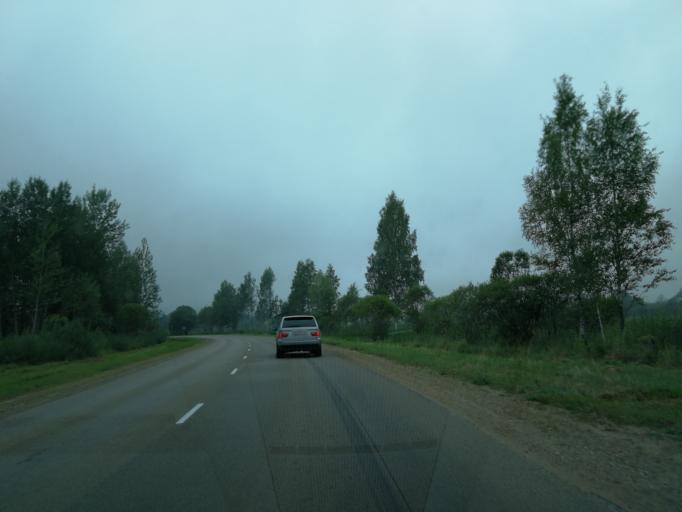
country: LV
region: Preilu Rajons
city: Preili
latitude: 56.3022
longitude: 26.7219
